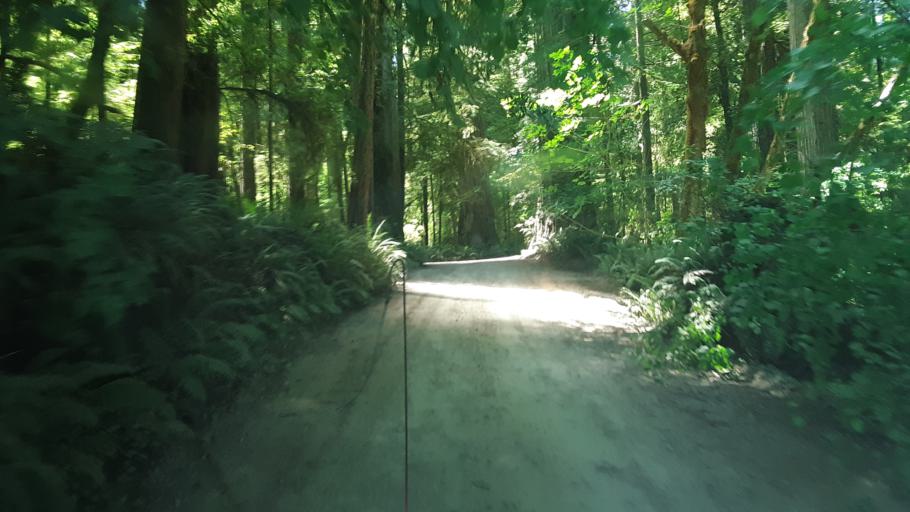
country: US
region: California
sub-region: Del Norte County
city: Bertsch-Oceanview
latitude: 41.8203
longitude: -124.1090
